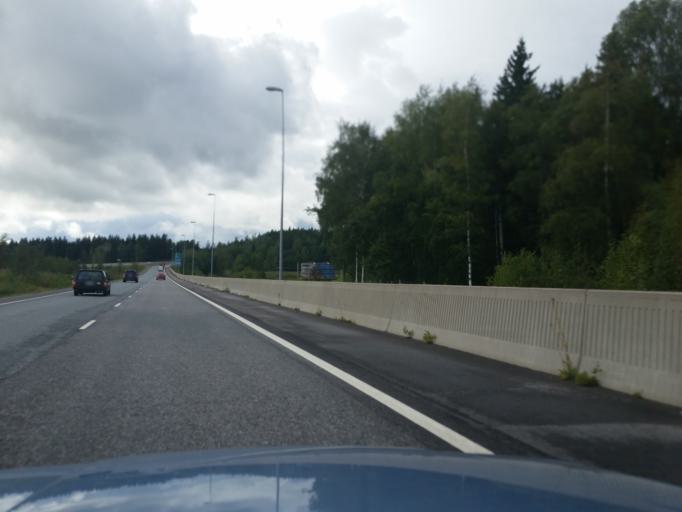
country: FI
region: Uusimaa
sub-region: Helsinki
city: Vihti
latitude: 60.3013
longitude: 24.2435
